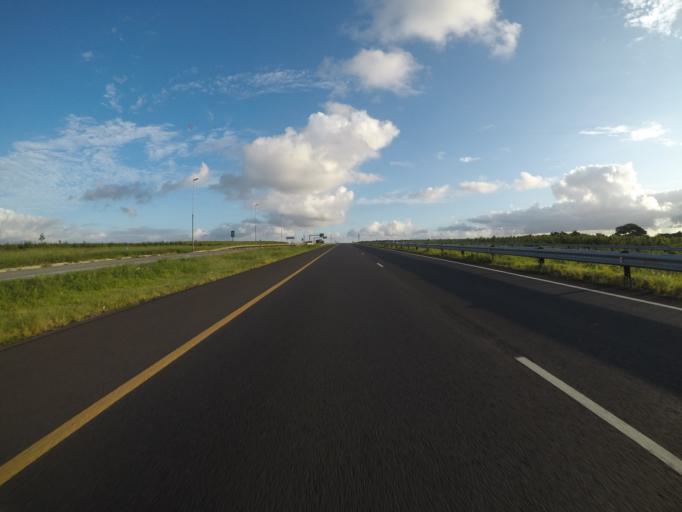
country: ZA
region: KwaZulu-Natal
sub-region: uThungulu District Municipality
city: KwaMbonambi
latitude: -28.5114
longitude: 32.1378
